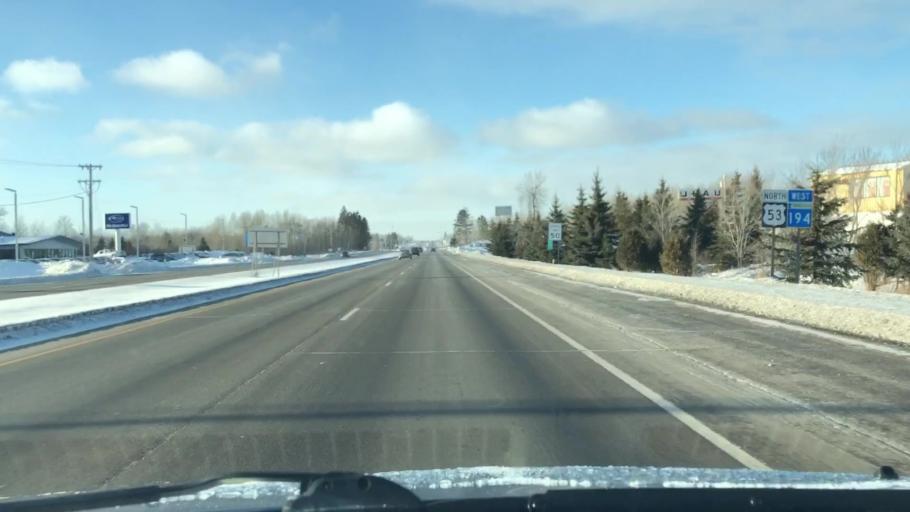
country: US
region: Minnesota
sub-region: Saint Louis County
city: Hermantown
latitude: 46.8158
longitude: -92.1761
